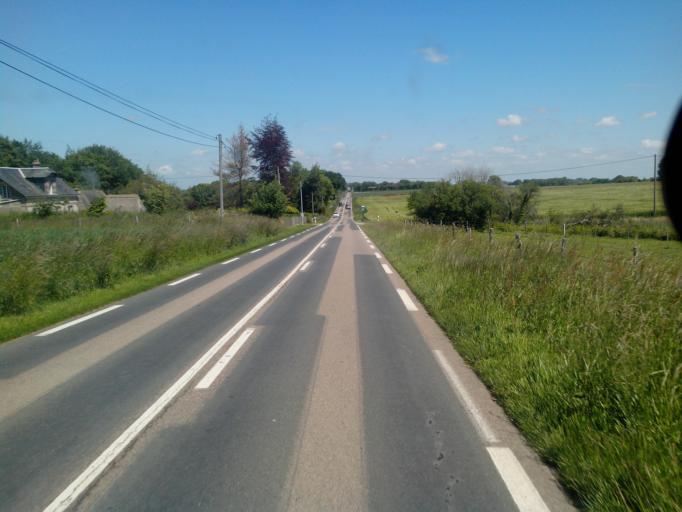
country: FR
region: Haute-Normandie
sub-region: Departement de la Seine-Maritime
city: Gonneville-la-Mallet
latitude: 49.6409
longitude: 0.2390
